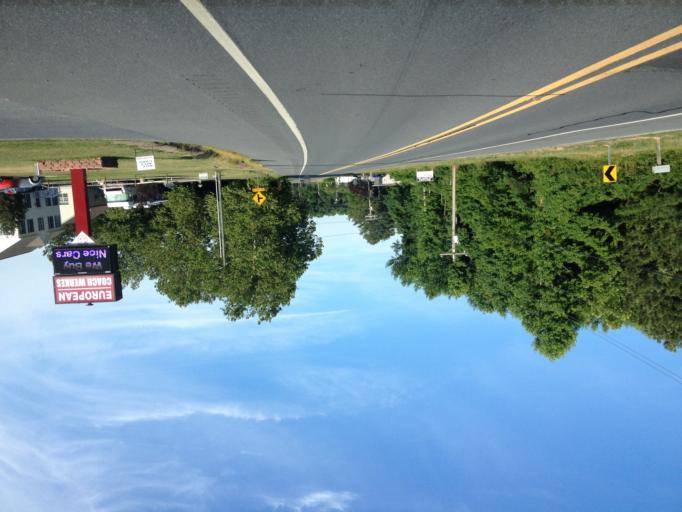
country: US
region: Delaware
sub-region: Sussex County
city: Selbyville
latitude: 38.4816
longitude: -75.1537
